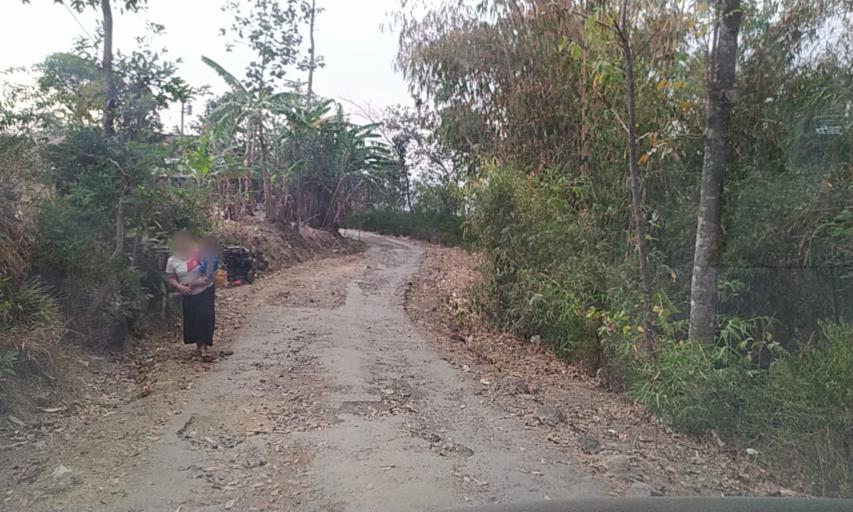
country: ID
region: Central Java
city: Randudongkal
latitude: -7.1416
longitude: 109.3747
